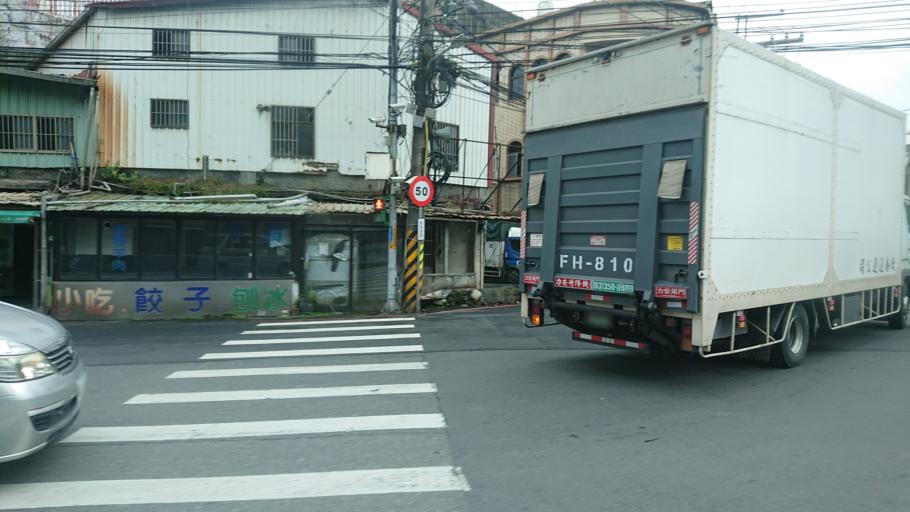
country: TW
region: Taiwan
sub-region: Taoyuan
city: Taoyuan
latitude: 24.9365
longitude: 121.3959
